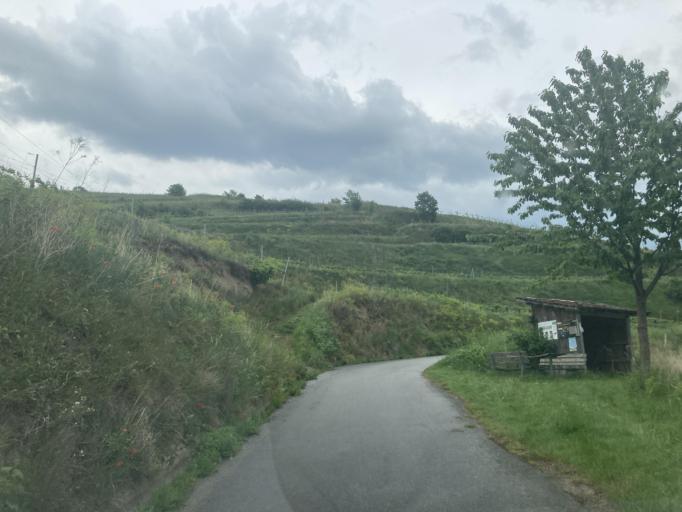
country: DE
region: Baden-Wuerttemberg
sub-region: Freiburg Region
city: Vogtsburg
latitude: 48.0887
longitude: 7.6554
